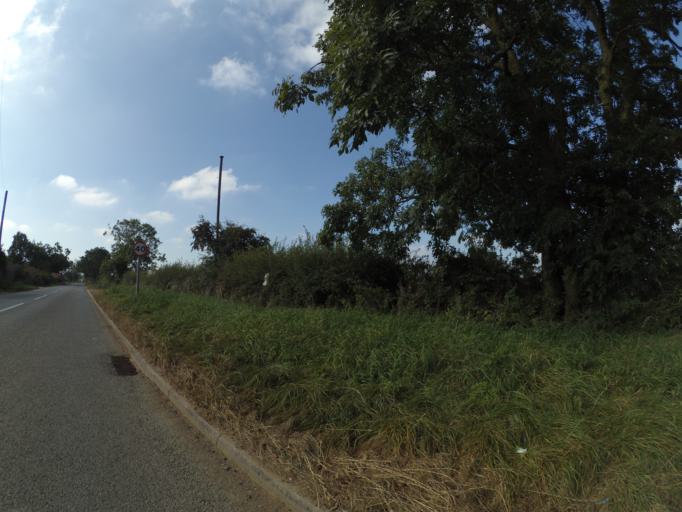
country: GB
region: England
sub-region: Warwickshire
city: Rugby
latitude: 52.3736
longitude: -1.2199
